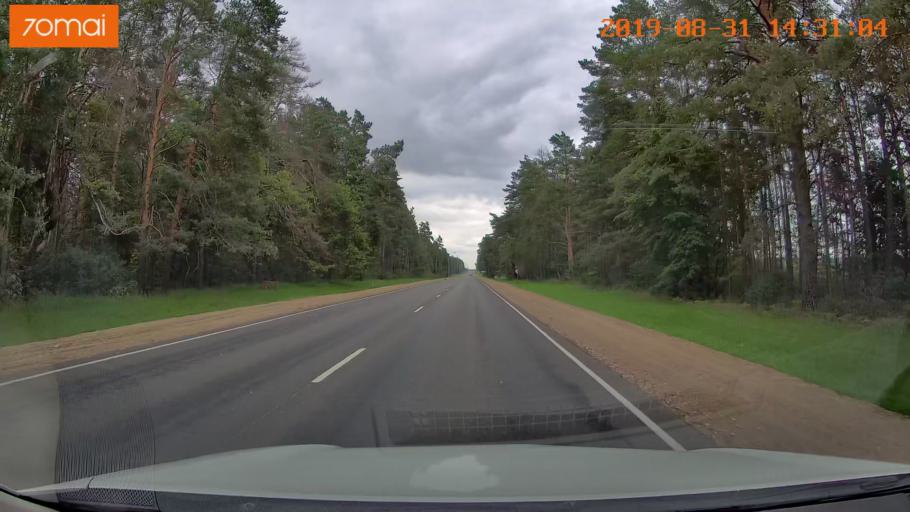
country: RU
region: Smolensk
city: Yekimovichi
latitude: 54.1358
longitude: 33.3652
